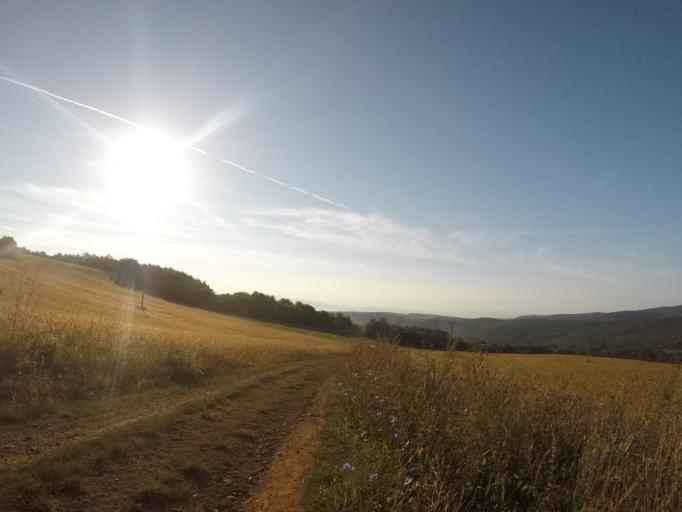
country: SK
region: Kosicky
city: Kosice
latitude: 48.7417
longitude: 21.1277
